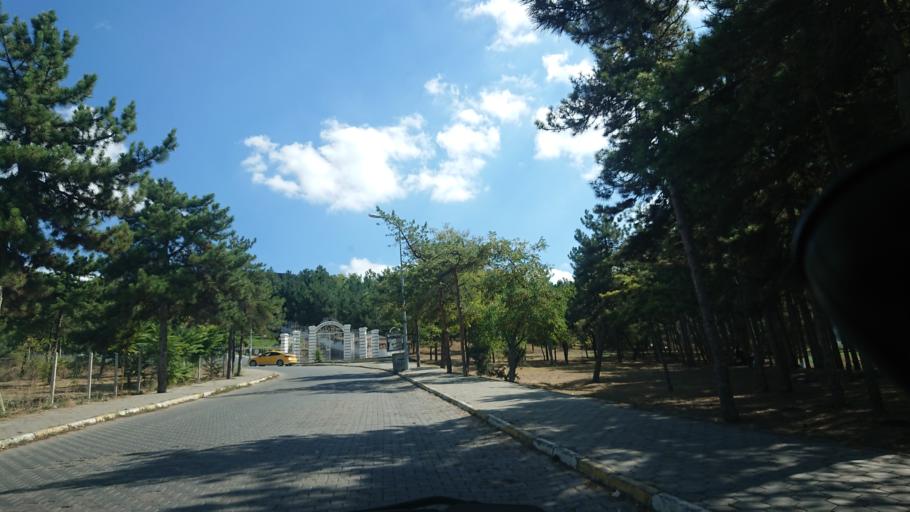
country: TR
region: Eskisehir
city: Eskisehir
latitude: 39.7584
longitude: 30.5304
